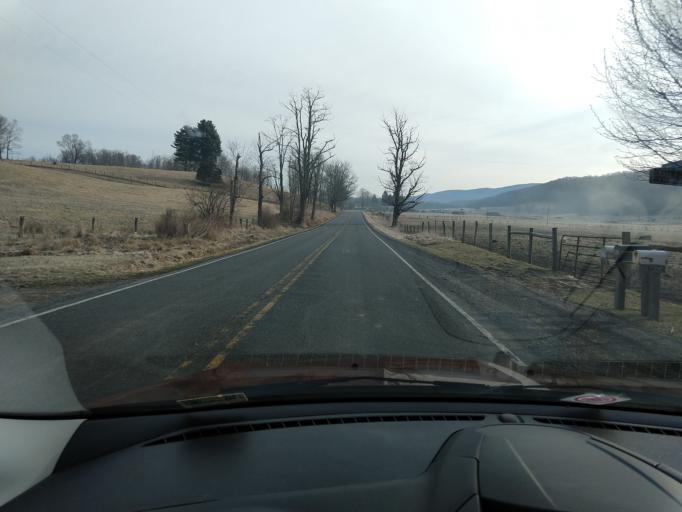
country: US
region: Virginia
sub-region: Highland County
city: Monterey
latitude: 38.4277
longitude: -79.5645
